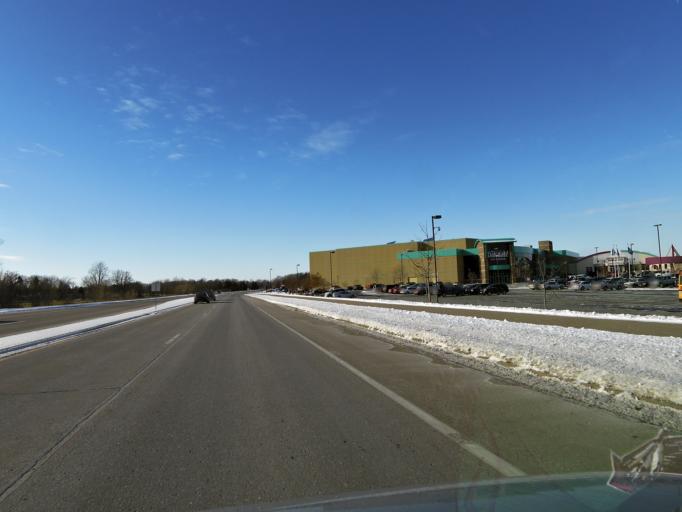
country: US
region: Minnesota
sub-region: Scott County
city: Prior Lake
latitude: 44.7237
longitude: -93.4756
